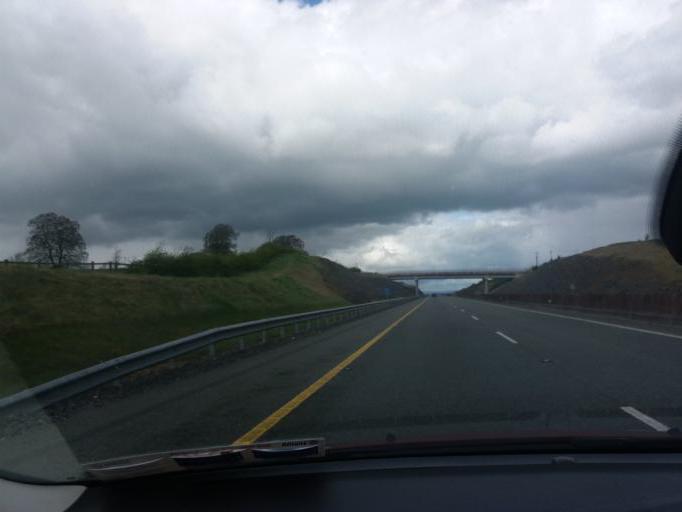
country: IE
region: Leinster
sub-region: Laois
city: Rathdowney
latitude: 52.8221
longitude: -7.4958
